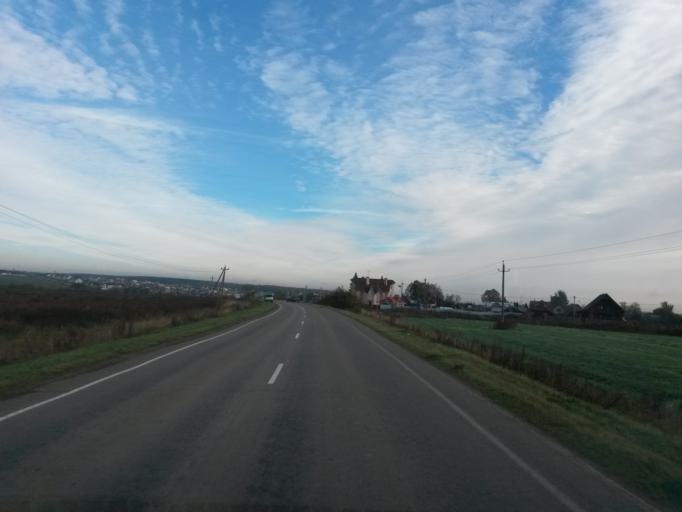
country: RU
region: Moskovskaya
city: Barybino
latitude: 55.2267
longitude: 37.7949
